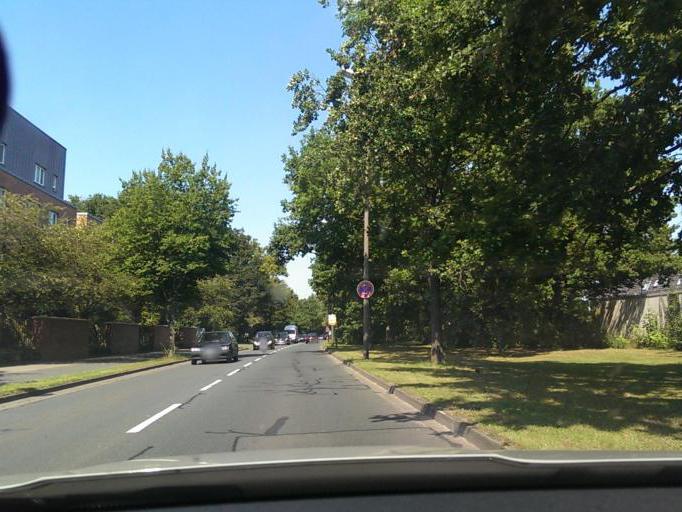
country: DE
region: Lower Saxony
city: Langenhagen
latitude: 52.4415
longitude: 9.7536
